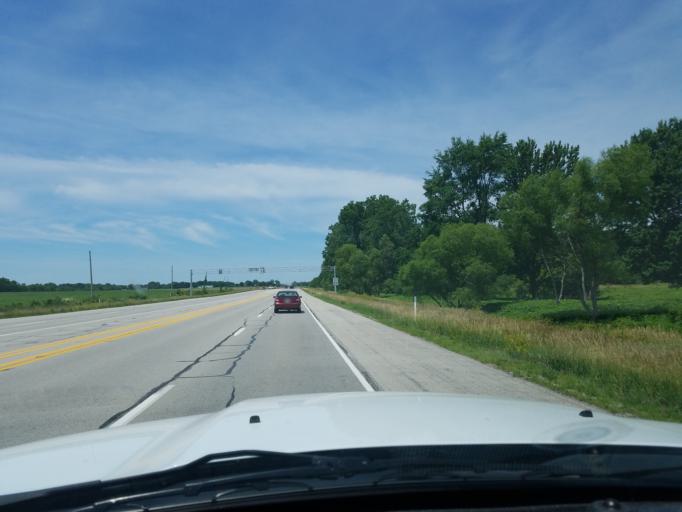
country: US
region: Indiana
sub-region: Delaware County
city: Daleville
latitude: 40.1137
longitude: -85.5013
